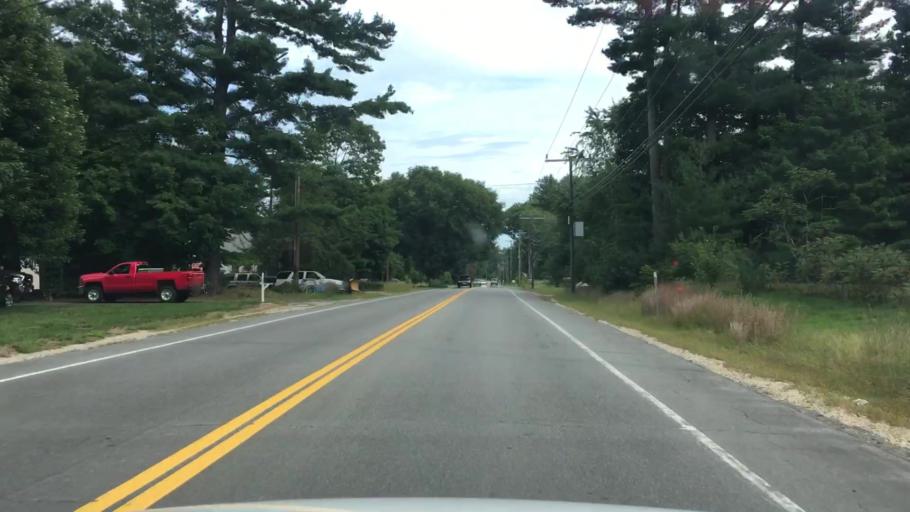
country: US
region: New Hampshire
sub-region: Strafford County
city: Madbury
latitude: 43.1916
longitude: -70.9270
